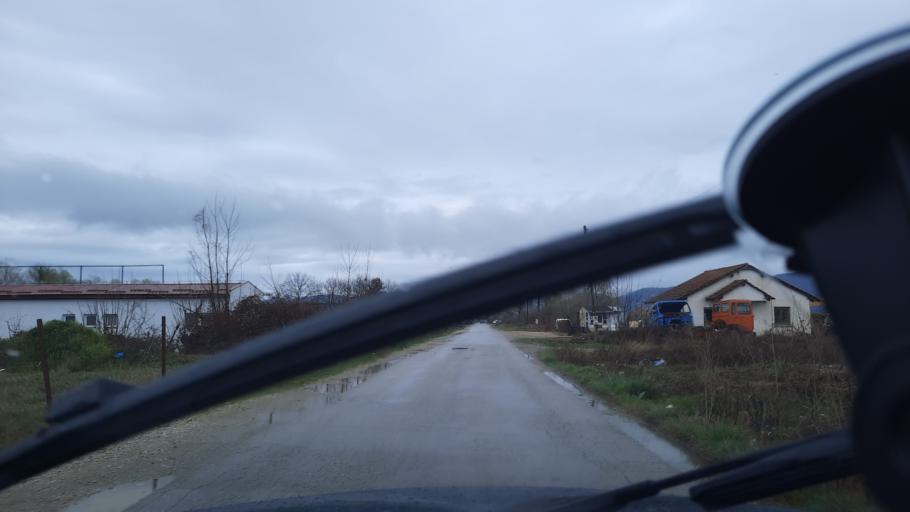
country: MK
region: Struga
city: Struga
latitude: 41.1995
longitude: 20.6818
